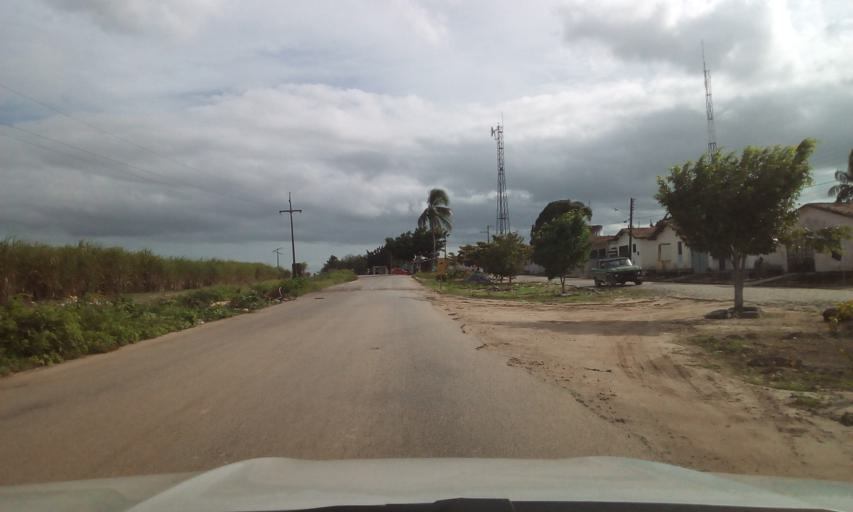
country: BR
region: Paraiba
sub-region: Santa Rita
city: Santa Rita
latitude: -6.9774
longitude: -34.9822
